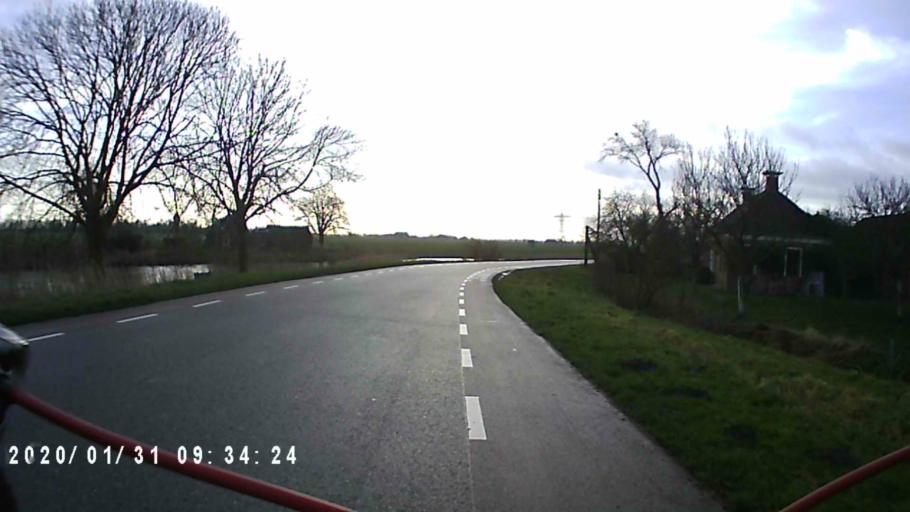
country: NL
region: Groningen
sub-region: Gemeente Winsum
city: Winsum
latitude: 53.3066
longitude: 6.4795
